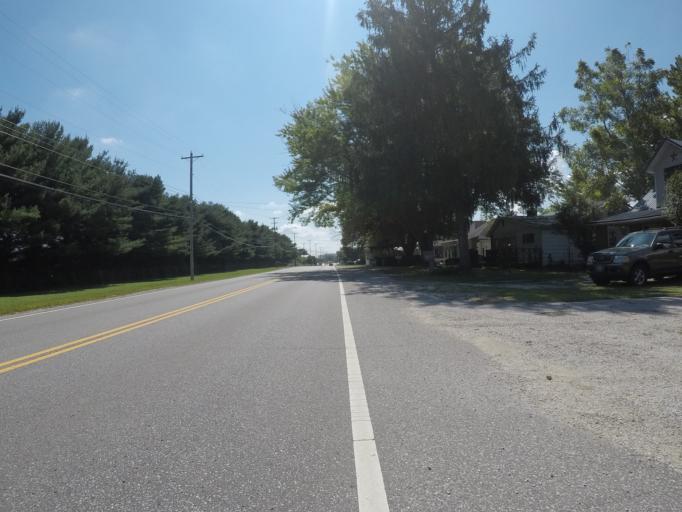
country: US
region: Ohio
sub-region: Lawrence County
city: South Point
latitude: 38.4241
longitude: -82.5909
